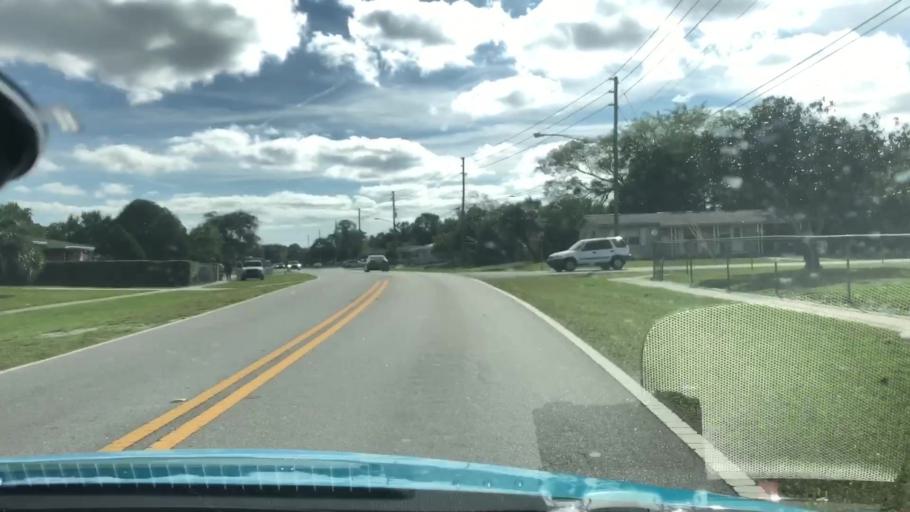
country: US
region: Florida
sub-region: Volusia County
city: Deltona
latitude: 28.9057
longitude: -81.2634
